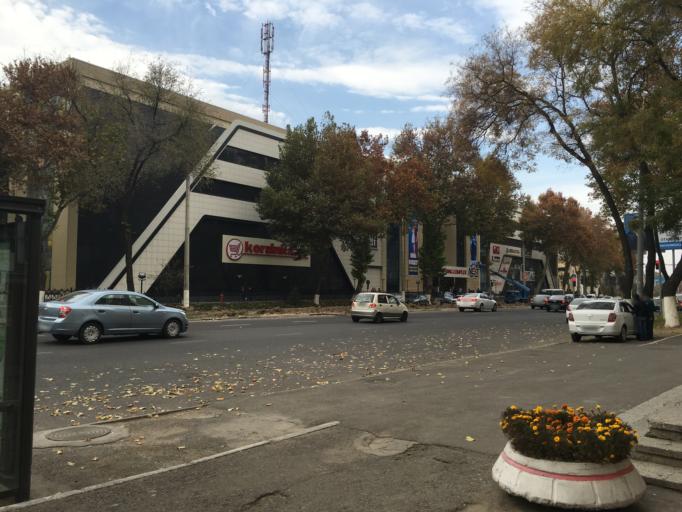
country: UZ
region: Toshkent Shahri
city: Tashkent
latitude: 41.2973
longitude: 69.2501
